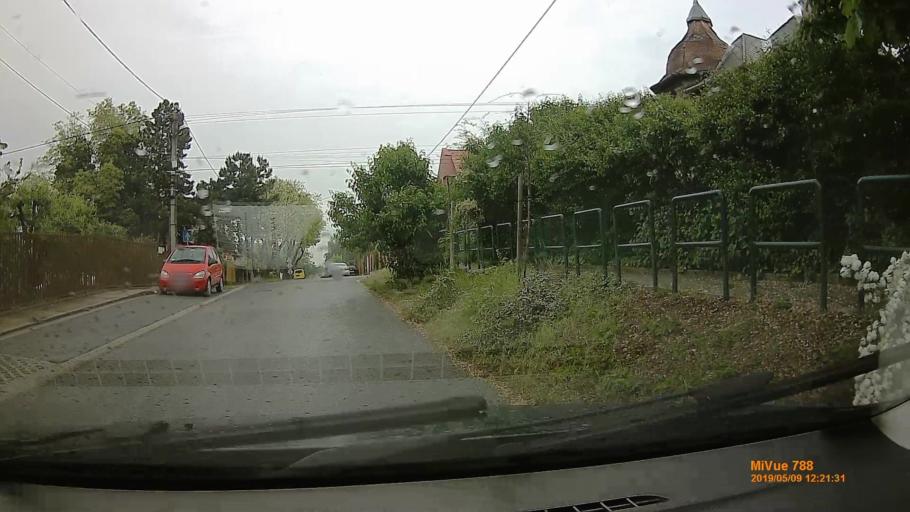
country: HU
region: Budapest
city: Budapest XVI. keruelet
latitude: 47.5181
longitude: 19.1663
